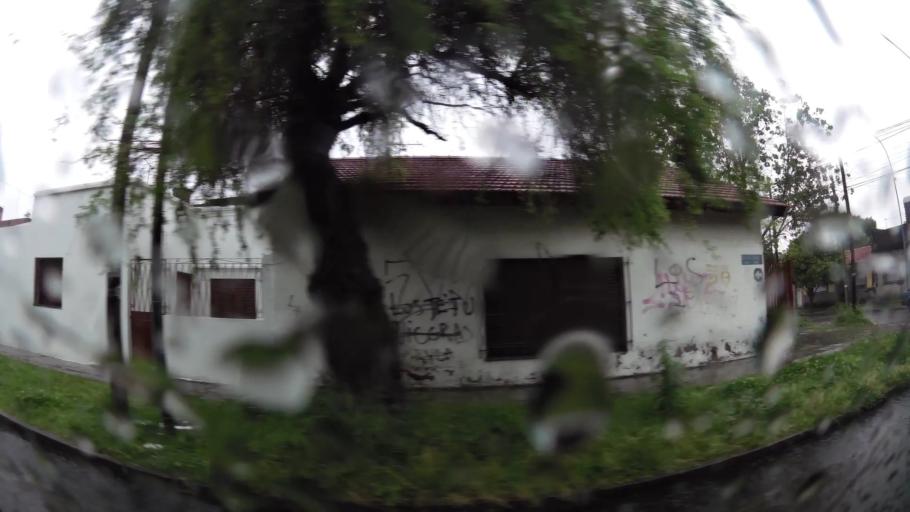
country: AR
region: Buenos Aires
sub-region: Partido de Lanus
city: Lanus
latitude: -34.7080
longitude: -58.4096
